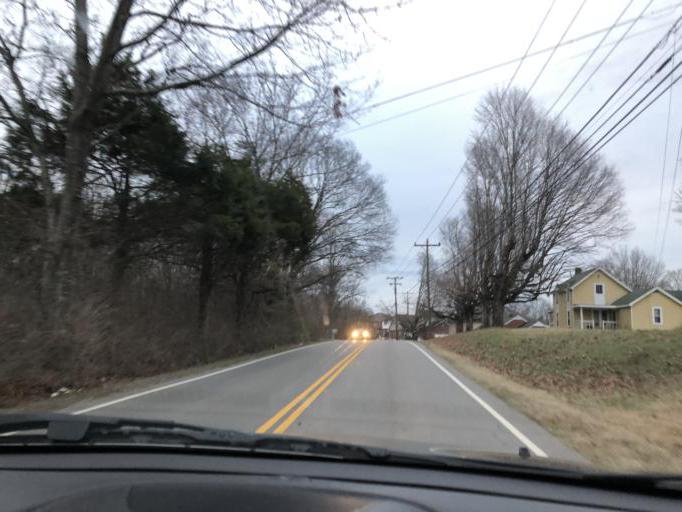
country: US
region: Tennessee
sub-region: Wilson County
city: Green Hill
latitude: 36.1888
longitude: -86.5907
